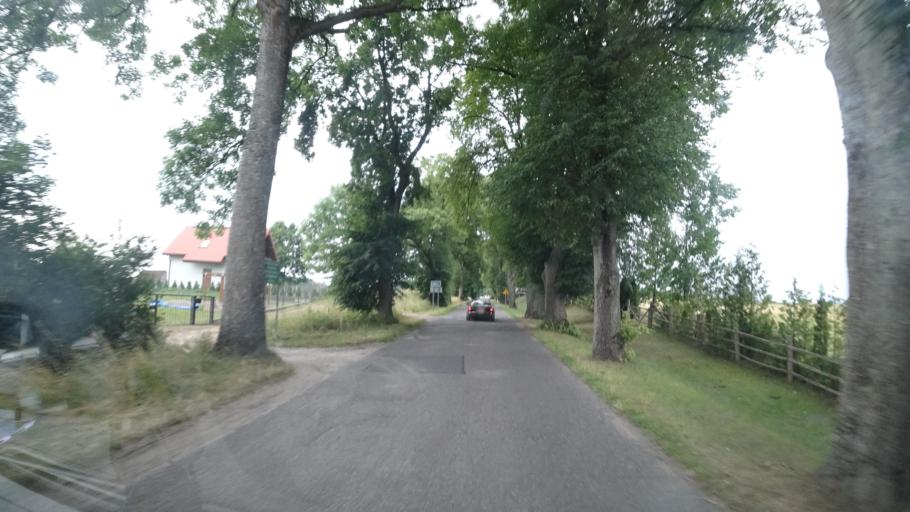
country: PL
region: Warmian-Masurian Voivodeship
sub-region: Powiat gizycki
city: Ryn
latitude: 53.9312
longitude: 21.5500
